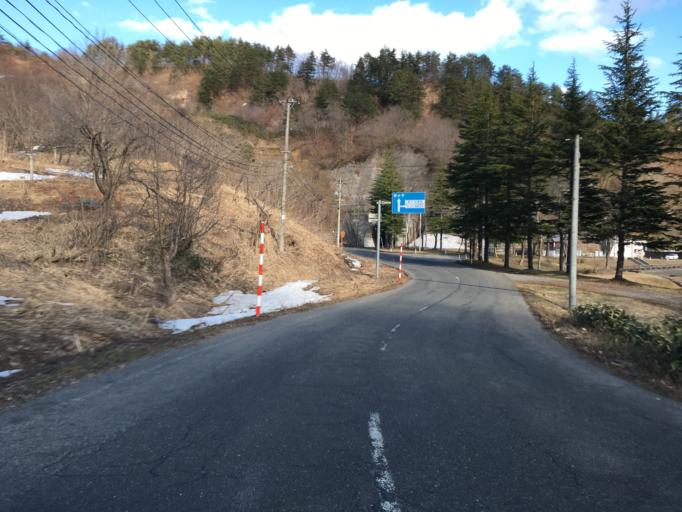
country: JP
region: Yamagata
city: Nagai
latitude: 37.9766
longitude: 139.9206
